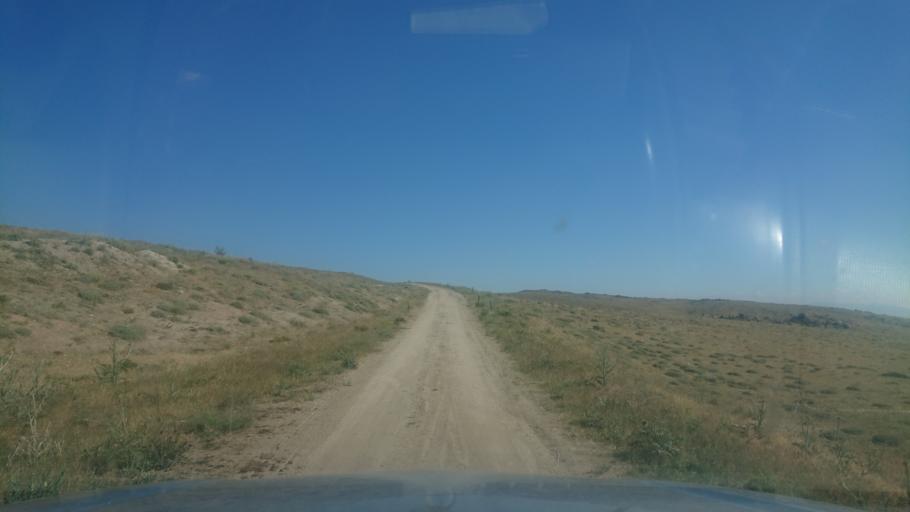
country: TR
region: Aksaray
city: Sariyahsi
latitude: 38.9170
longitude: 33.8548
